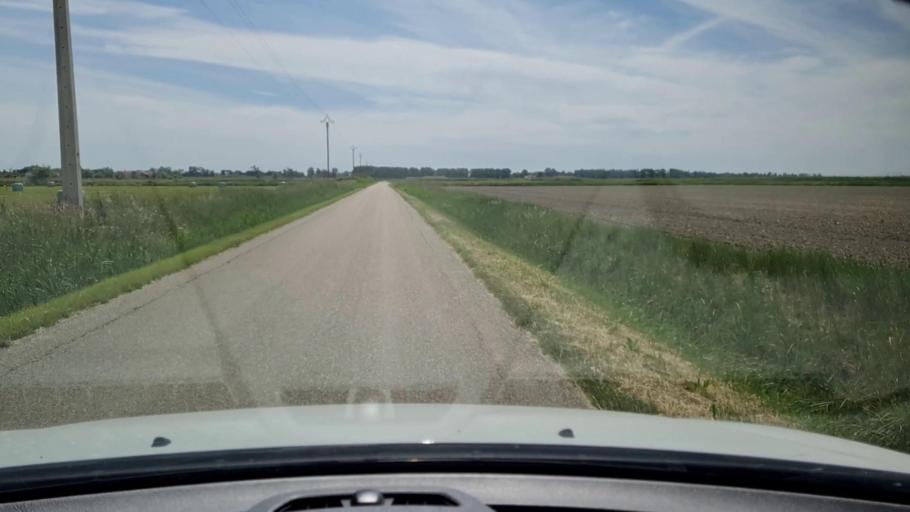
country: FR
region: Languedoc-Roussillon
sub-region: Departement du Gard
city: Saint-Gilles
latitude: 43.5936
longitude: 4.4571
